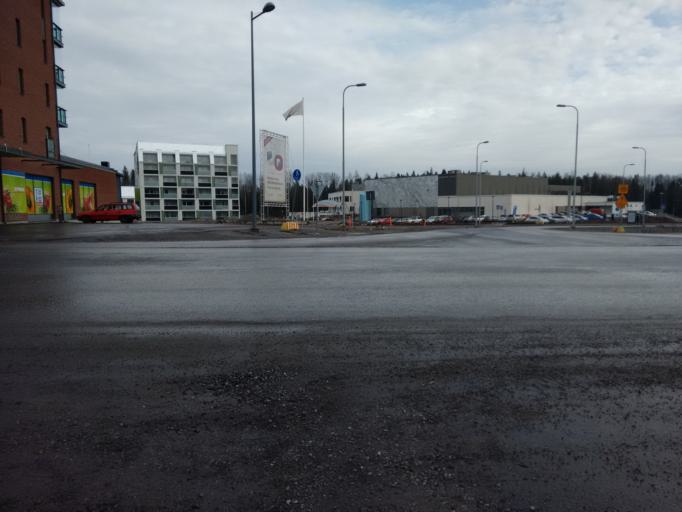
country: FI
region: Pirkanmaa
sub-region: Tampere
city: Tampere
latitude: 61.4307
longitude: 23.8127
